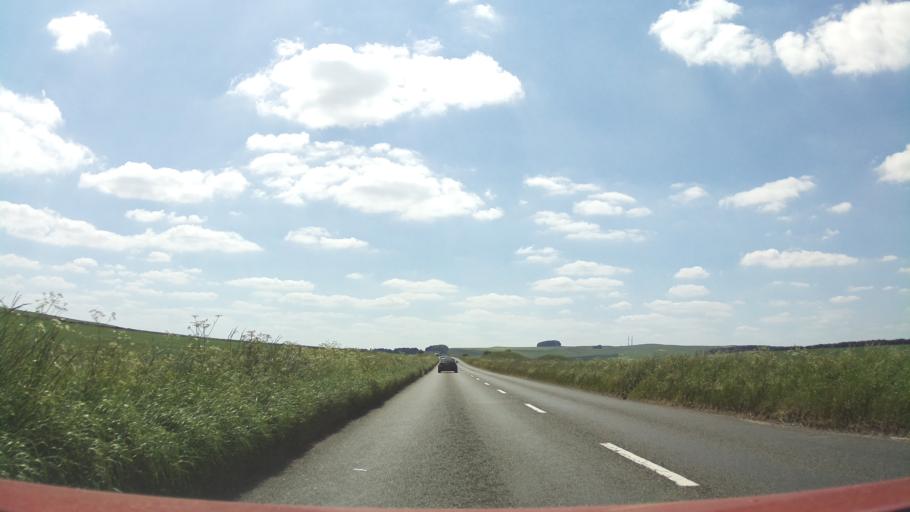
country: GB
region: England
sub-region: Wiltshire
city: Avebury
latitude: 51.4076
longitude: -1.9126
